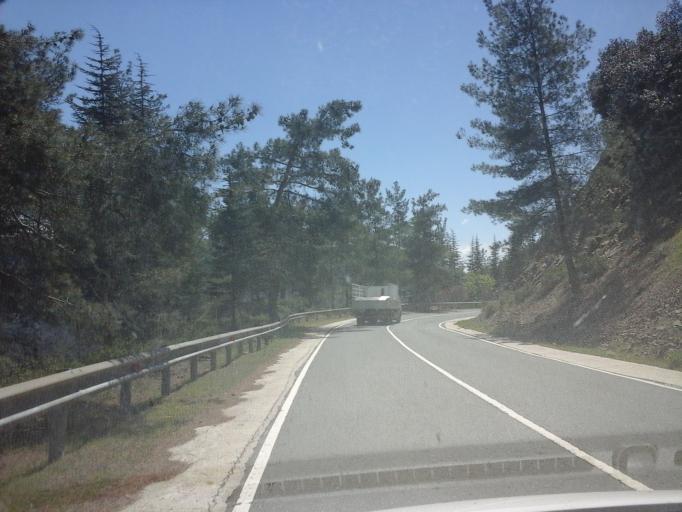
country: CY
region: Lefkosia
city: Kakopetria
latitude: 34.9892
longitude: 32.7886
